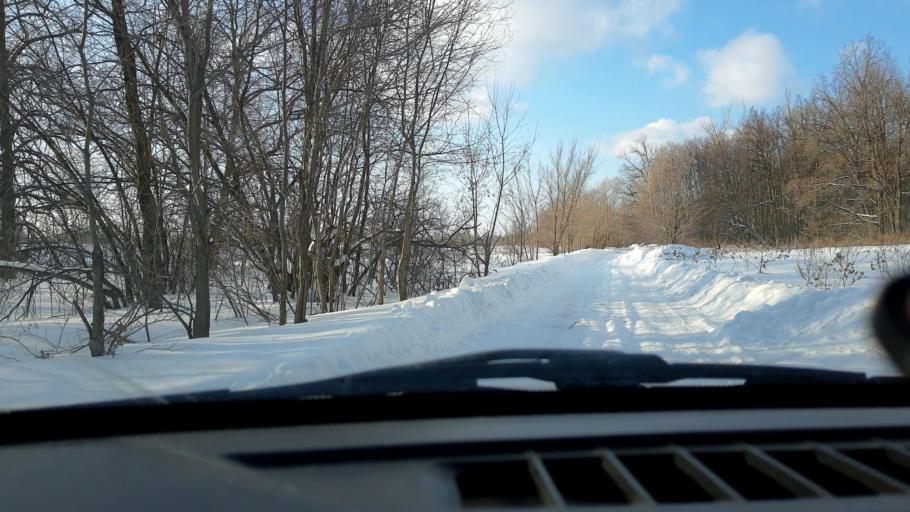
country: RU
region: Bashkortostan
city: Ufa
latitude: 54.6317
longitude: 56.0073
